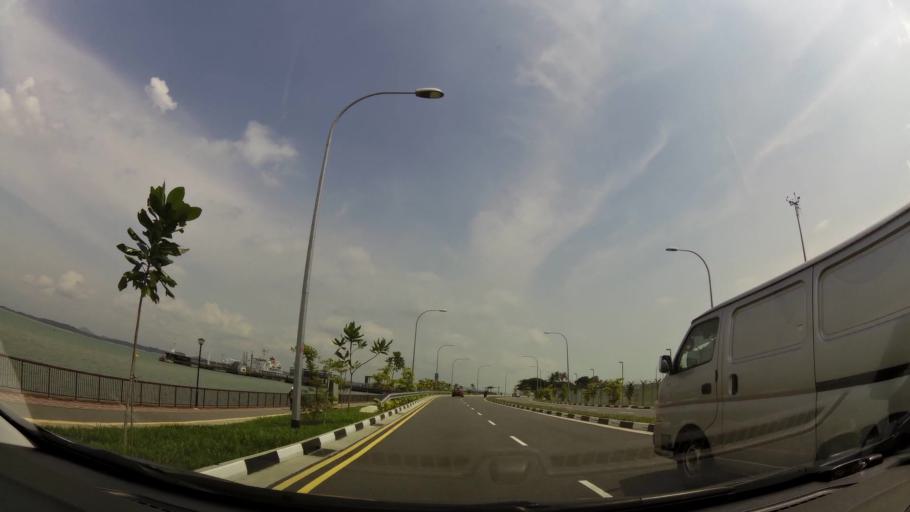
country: MY
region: Johor
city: Kampung Pasir Gudang Baru
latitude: 1.3897
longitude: 103.9967
